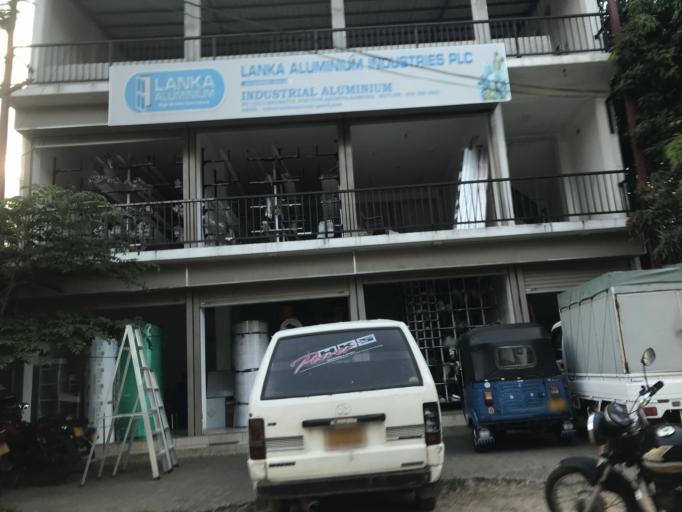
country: LK
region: Western
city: Gampaha
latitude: 7.1017
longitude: 79.9909
